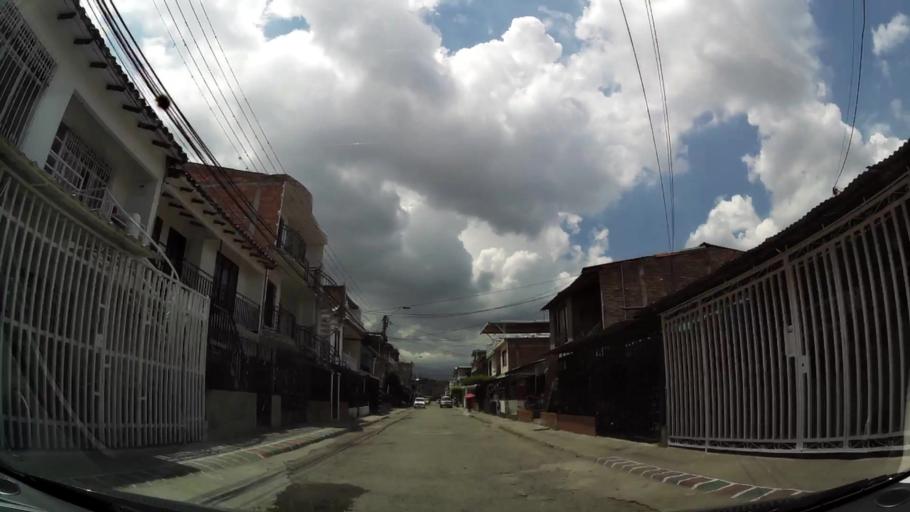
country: CO
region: Valle del Cauca
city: Cali
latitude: 3.4735
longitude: -76.4834
